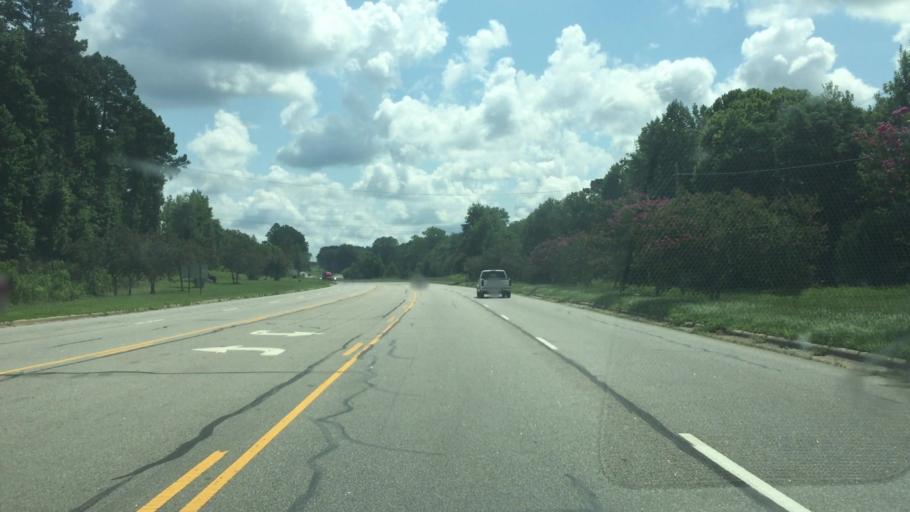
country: US
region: North Carolina
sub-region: Anson County
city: Wadesboro
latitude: 34.9632
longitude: -80.0407
